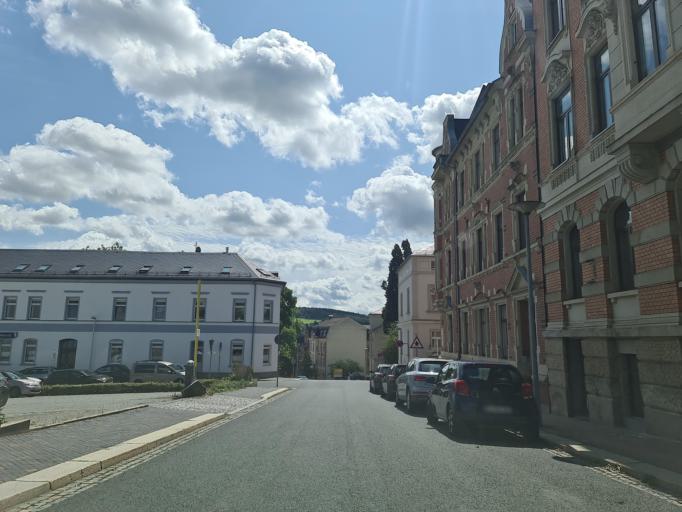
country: DE
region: Saxony
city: Plauen
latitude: 50.4967
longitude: 12.1410
